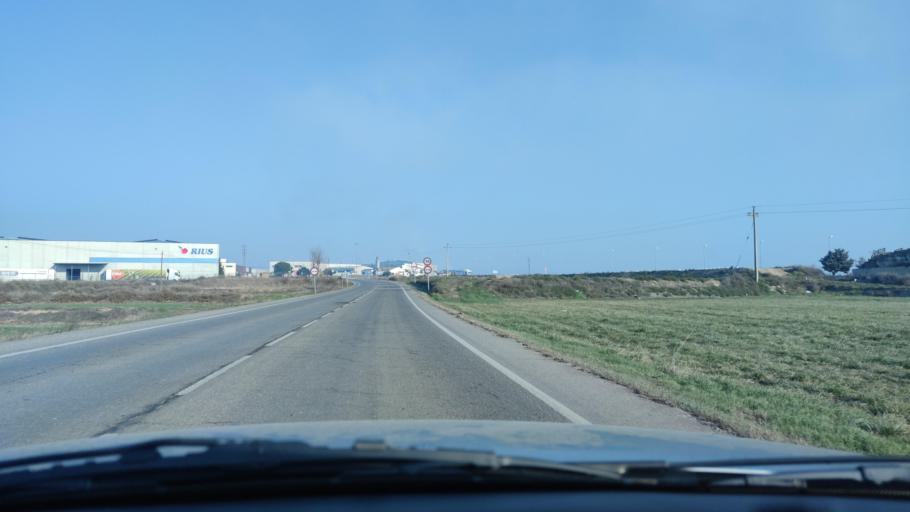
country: ES
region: Catalonia
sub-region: Provincia de Lleida
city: Torrefarrera
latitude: 41.6745
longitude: 0.6295
